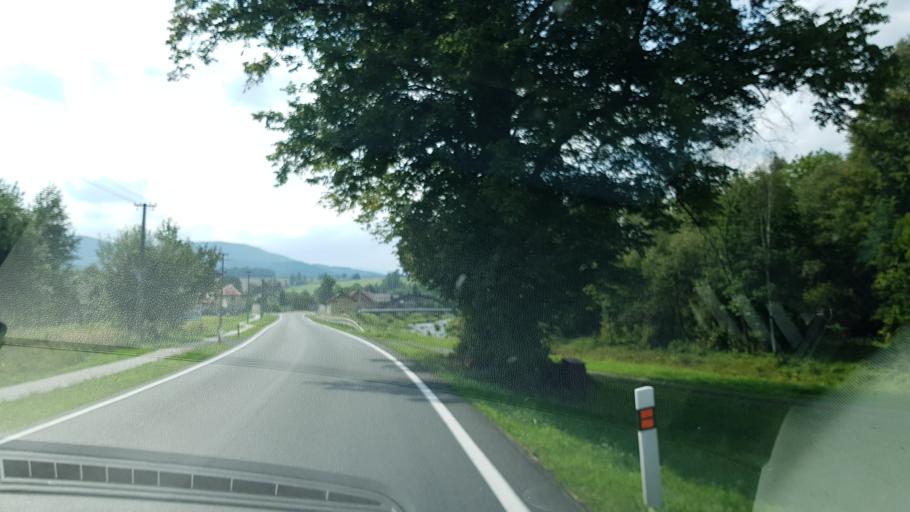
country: CZ
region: Olomoucky
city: Pisecna
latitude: 50.2806
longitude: 17.2863
